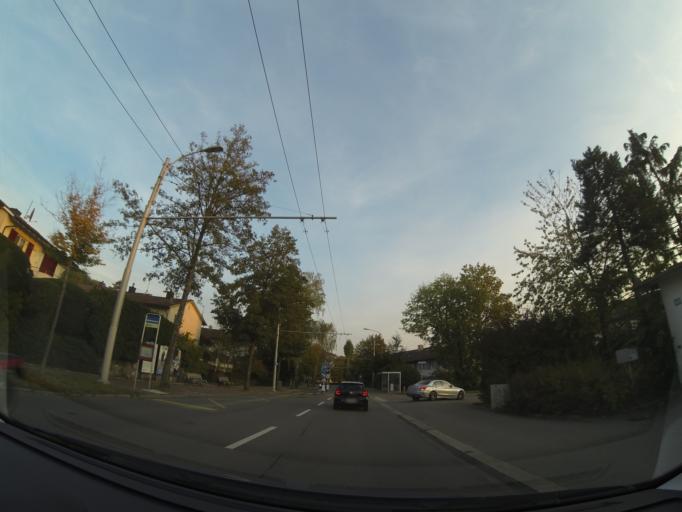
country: CH
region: Zurich
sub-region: Bezirk Zuerich
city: Zuerich (Kreis 10) / Ruetihof
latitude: 47.4108
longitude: 8.4858
